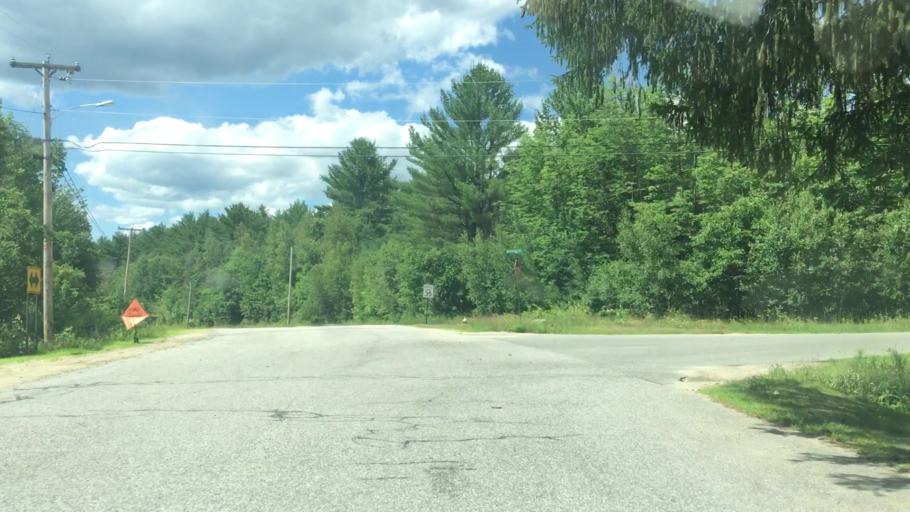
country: US
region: Maine
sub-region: Franklin County
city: Jay
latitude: 44.5353
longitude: -70.2267
